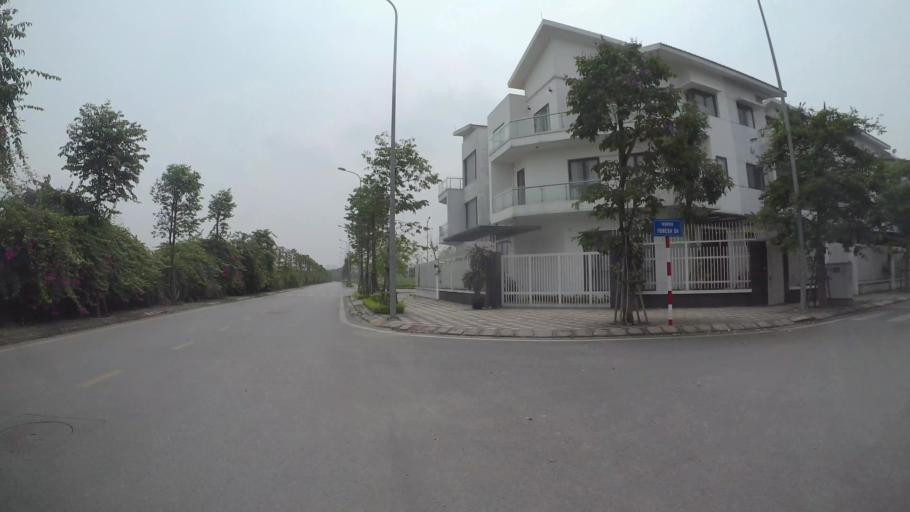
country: VN
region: Ha Noi
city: Cau Dien
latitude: 21.0287
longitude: 105.7484
